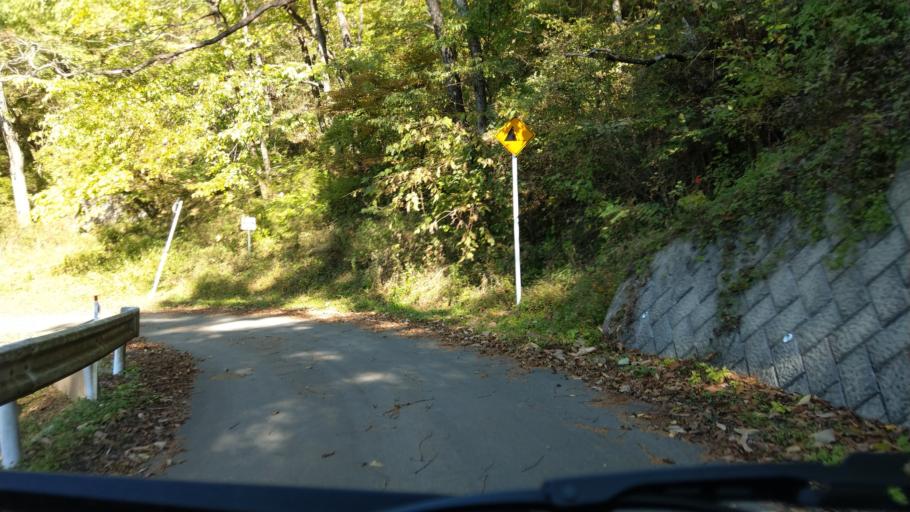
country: JP
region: Nagano
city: Komoro
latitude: 36.3765
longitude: 138.4190
